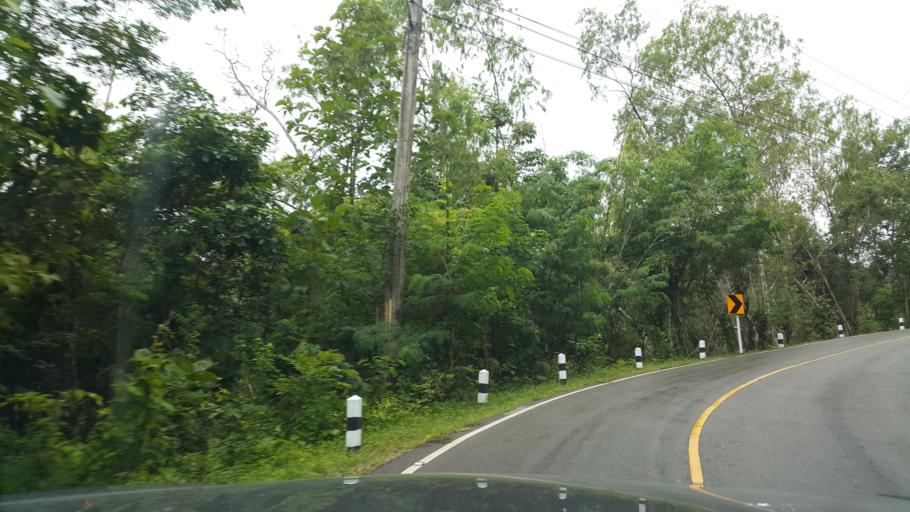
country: TH
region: Chiang Mai
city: Samoeng
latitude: 18.8527
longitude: 98.6844
